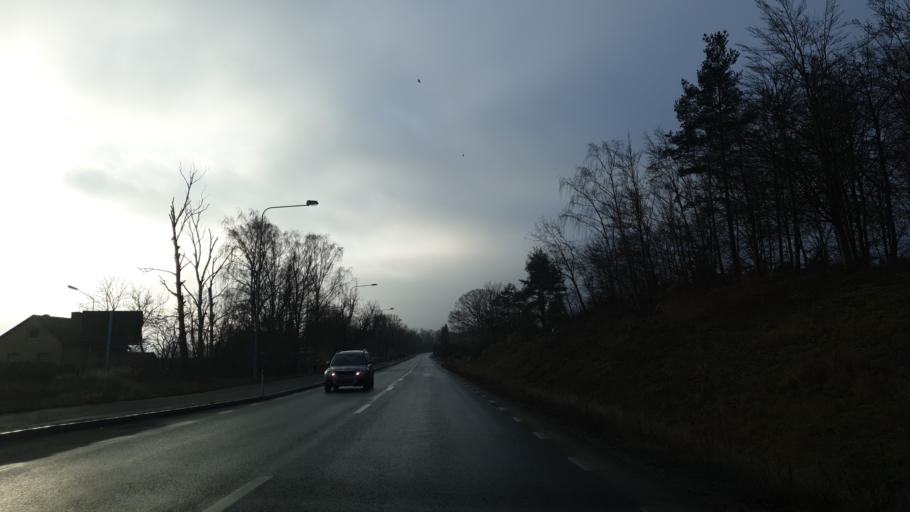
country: SE
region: Blekinge
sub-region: Karlshamns Kommun
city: Morrum
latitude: 56.1632
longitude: 14.6804
